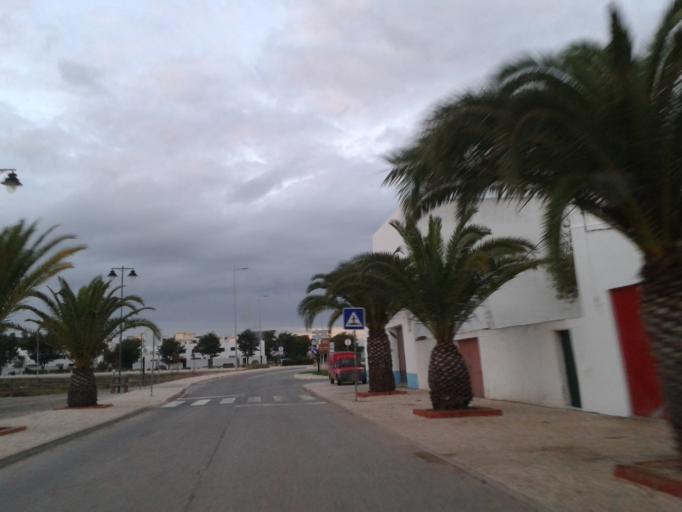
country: PT
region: Faro
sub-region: Castro Marim
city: Castro Marim
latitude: 37.2200
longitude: -7.4444
